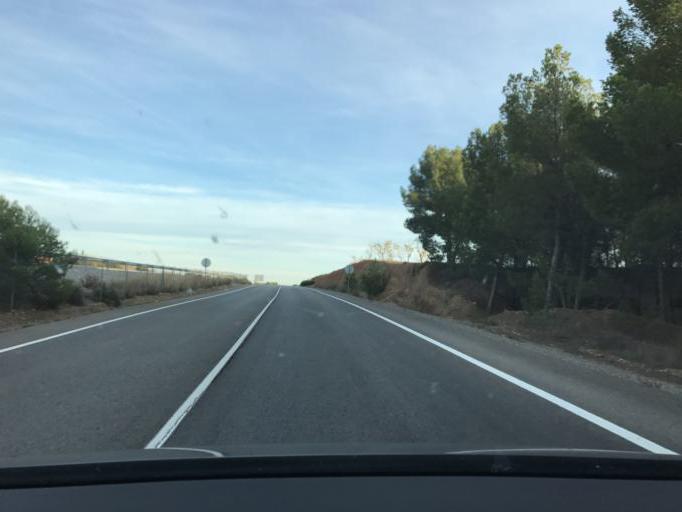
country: ES
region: Andalusia
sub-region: Provincia de Granada
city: Albunan
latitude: 37.2653
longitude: -3.0918
